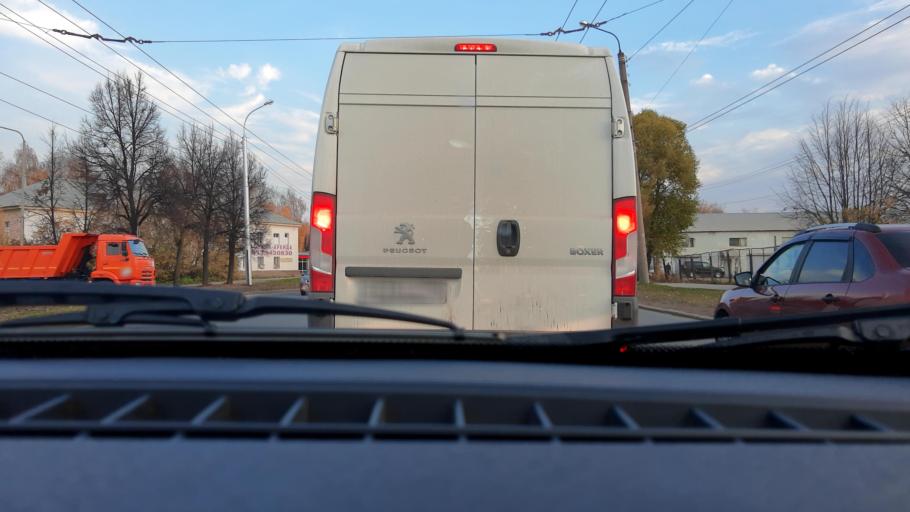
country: RU
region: Bashkortostan
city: Ufa
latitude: 54.7892
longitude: 56.1393
